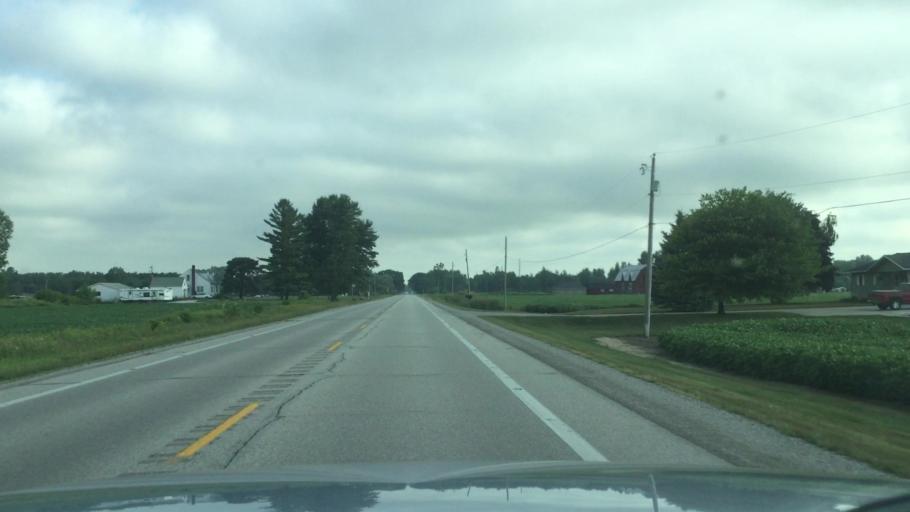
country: US
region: Michigan
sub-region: Saginaw County
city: Birch Run
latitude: 43.2599
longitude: -83.7356
